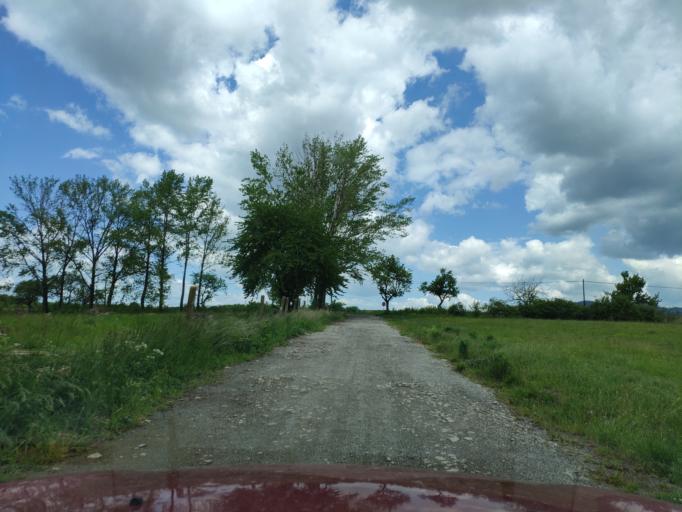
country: SK
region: Kosicky
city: Kosice
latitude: 48.8454
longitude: 21.3252
